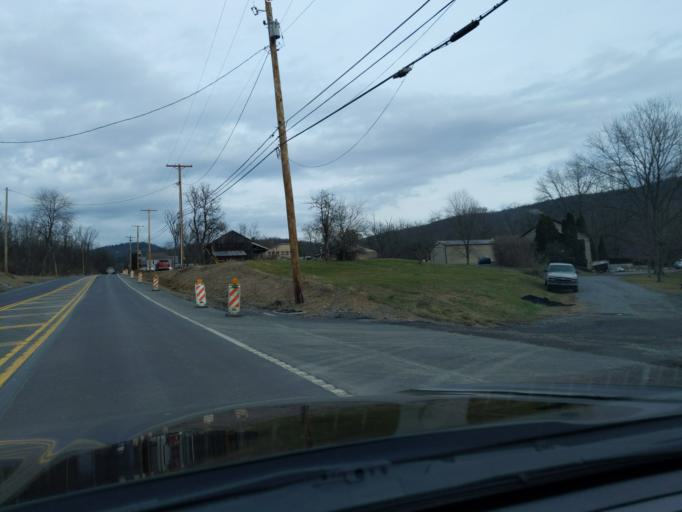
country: US
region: Pennsylvania
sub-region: Blair County
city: Williamsburg
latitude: 40.4735
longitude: -78.2798
